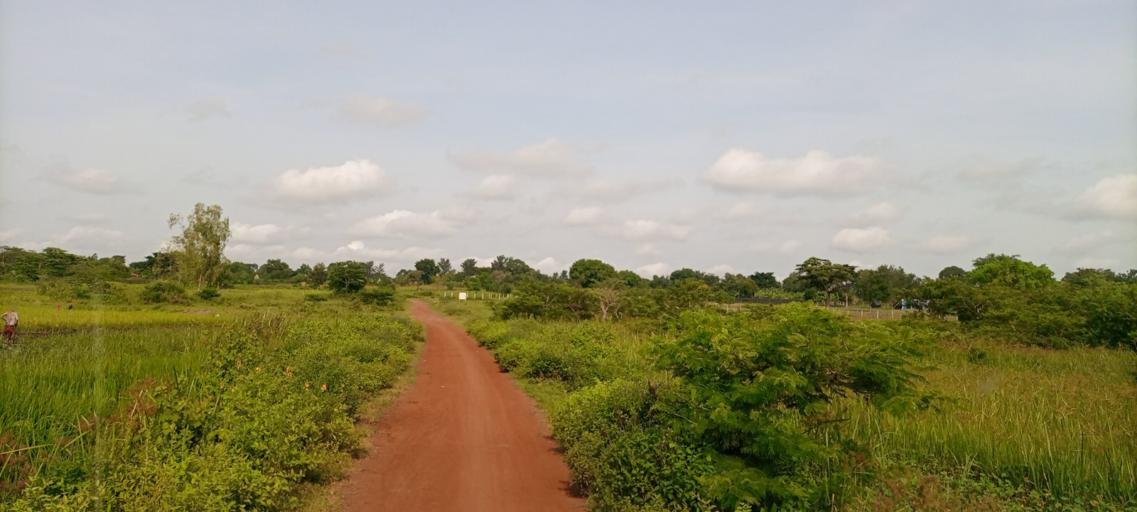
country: UG
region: Eastern Region
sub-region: Kibuku District
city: Kibuku
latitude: 1.0970
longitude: 33.7696
